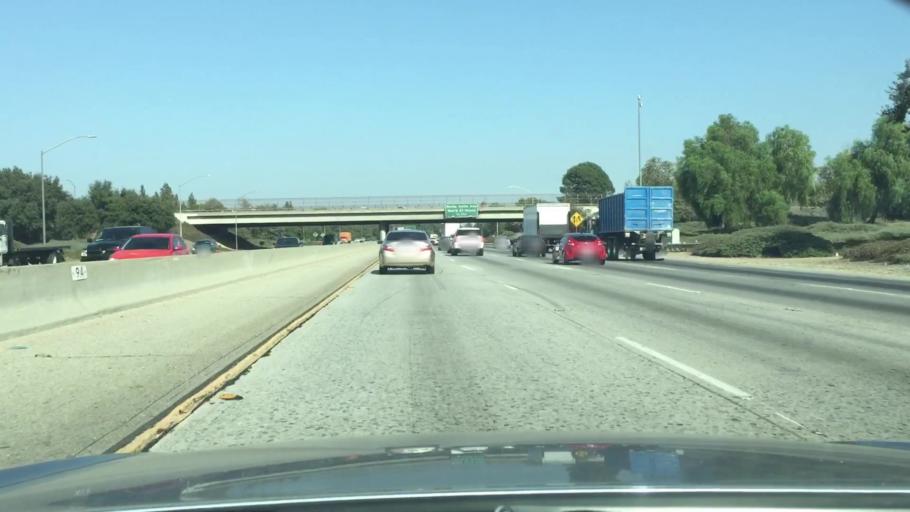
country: US
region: California
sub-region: Los Angeles County
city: South El Monte
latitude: 34.0418
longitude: -118.0662
